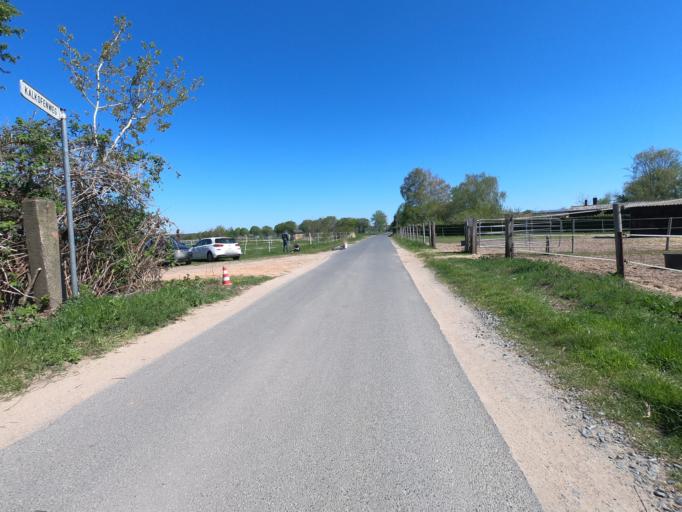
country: DE
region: Hesse
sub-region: Regierungsbezirk Darmstadt
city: Erzhausen
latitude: 49.9165
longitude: 8.6668
